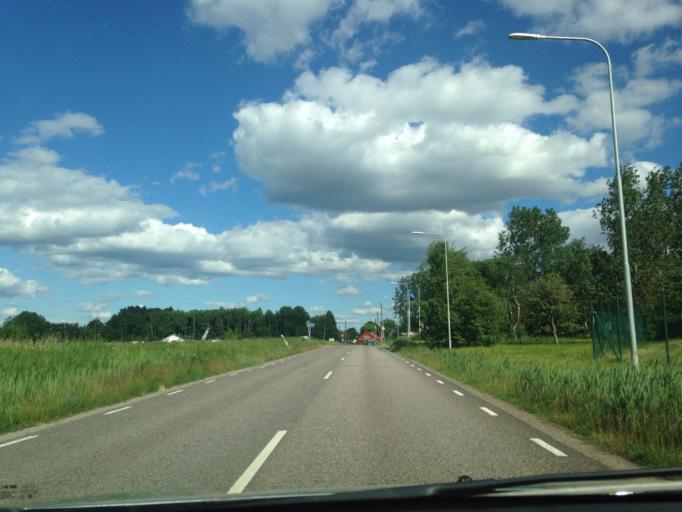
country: SE
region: Vaestra Goetaland
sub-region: Goteborg
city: Majorna
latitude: 57.7738
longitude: 11.9003
